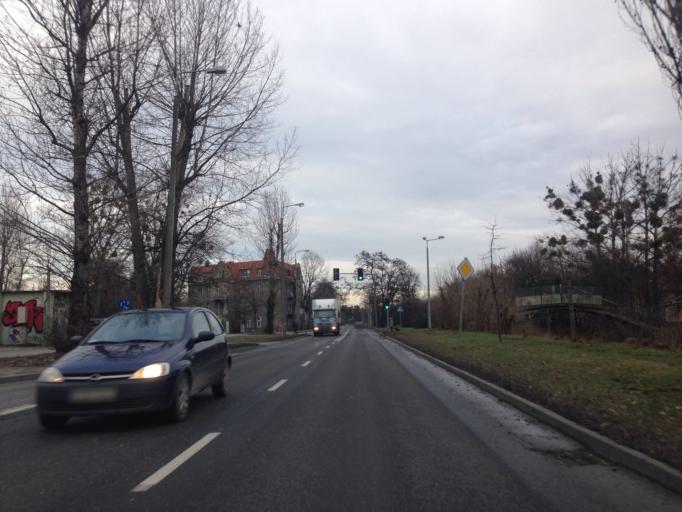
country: PL
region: Kujawsko-Pomorskie
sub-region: Torun
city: Torun
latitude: 53.0192
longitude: 18.6221
